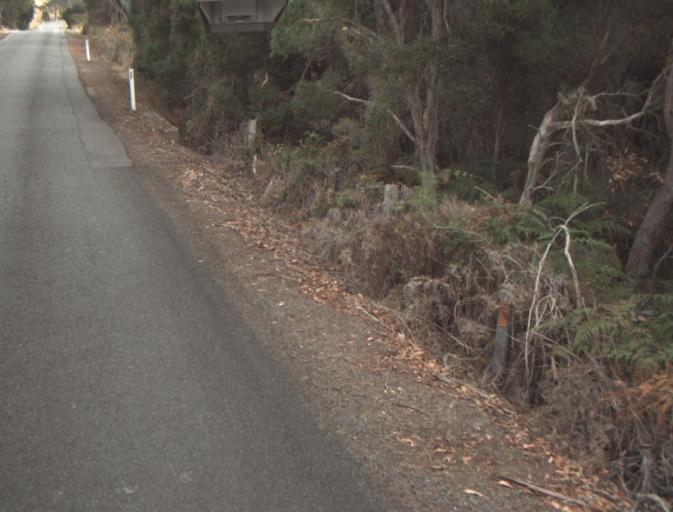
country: AU
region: Tasmania
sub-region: Launceston
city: Mayfield
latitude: -41.2825
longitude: 147.0278
